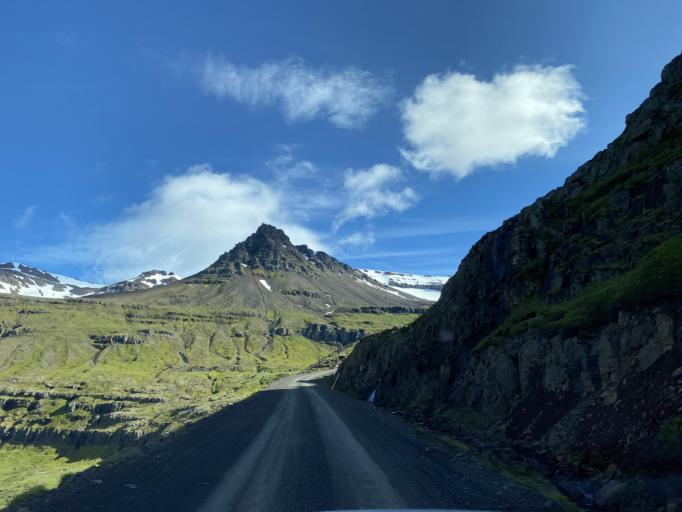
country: IS
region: East
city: Eskifjoerdur
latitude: 65.1811
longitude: -14.0852
